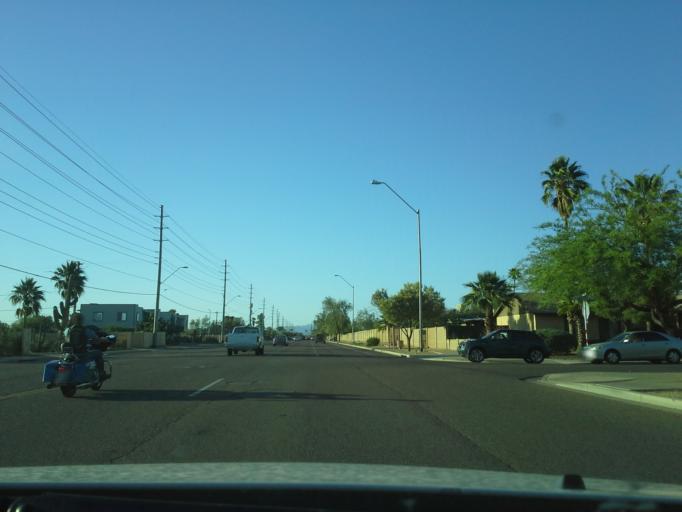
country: US
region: Arizona
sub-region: Maricopa County
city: Paradise Valley
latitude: 33.6439
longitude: -112.0134
